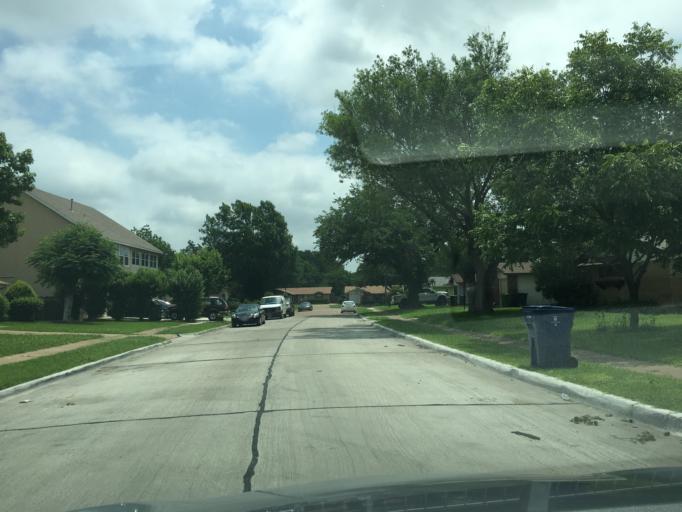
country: US
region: Texas
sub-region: Dallas County
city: Garland
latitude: 32.9210
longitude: -96.6766
